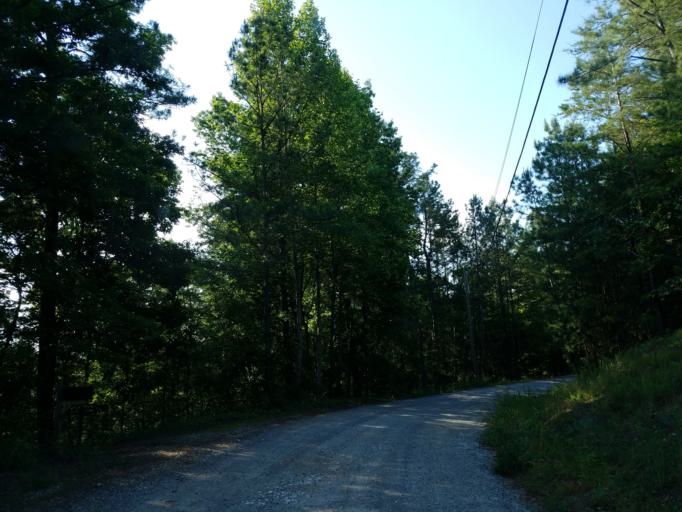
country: US
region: Georgia
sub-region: Pickens County
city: Nelson
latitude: 34.3712
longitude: -84.3413
